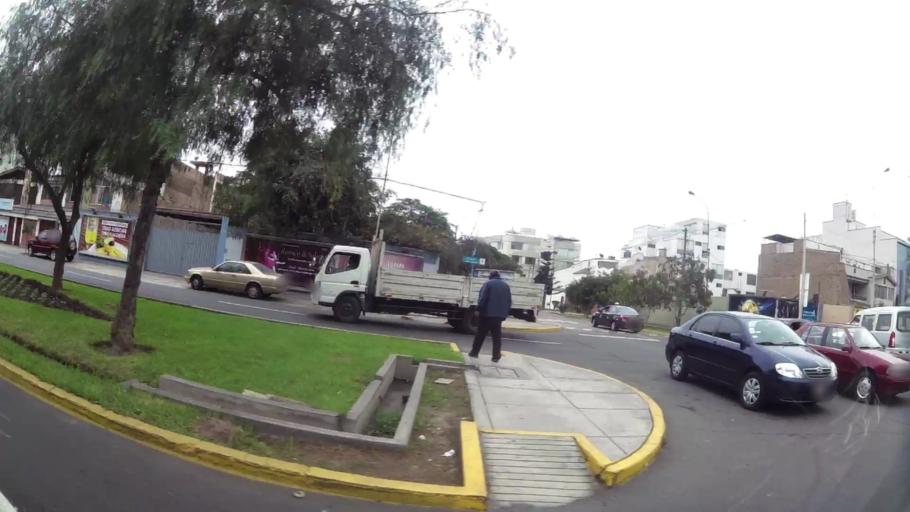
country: PE
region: Lima
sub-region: Lima
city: San Luis
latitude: -12.1043
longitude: -76.9935
